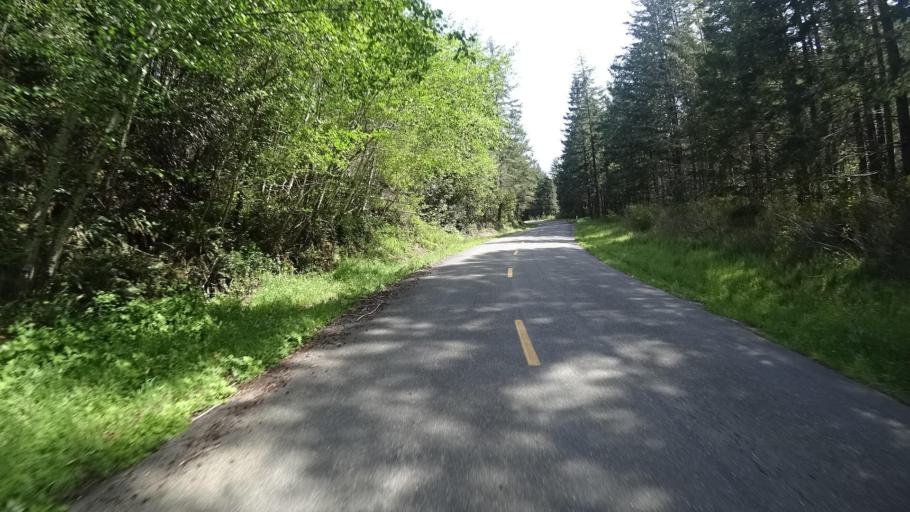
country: US
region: California
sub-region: Humboldt County
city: Rio Dell
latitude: 40.4575
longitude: -123.8038
